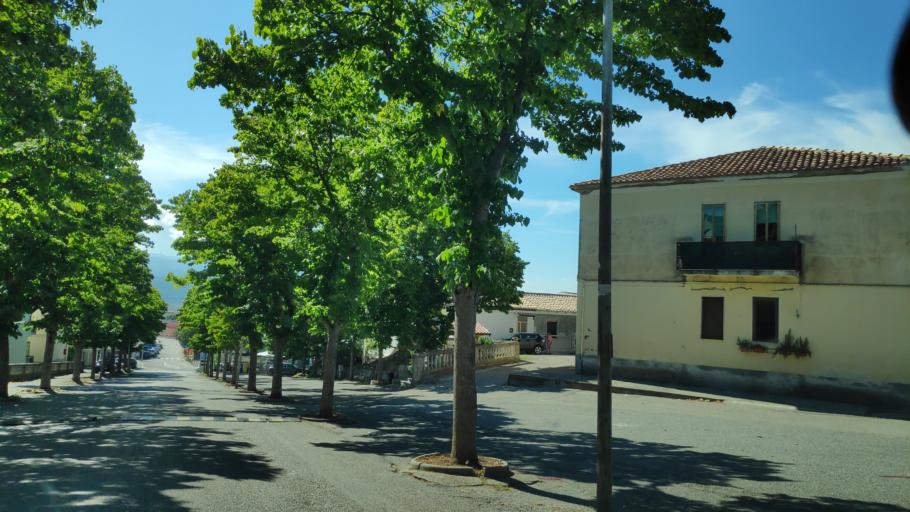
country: IT
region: Calabria
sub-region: Provincia di Catanzaro
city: Squillace
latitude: 38.7807
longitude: 16.5158
